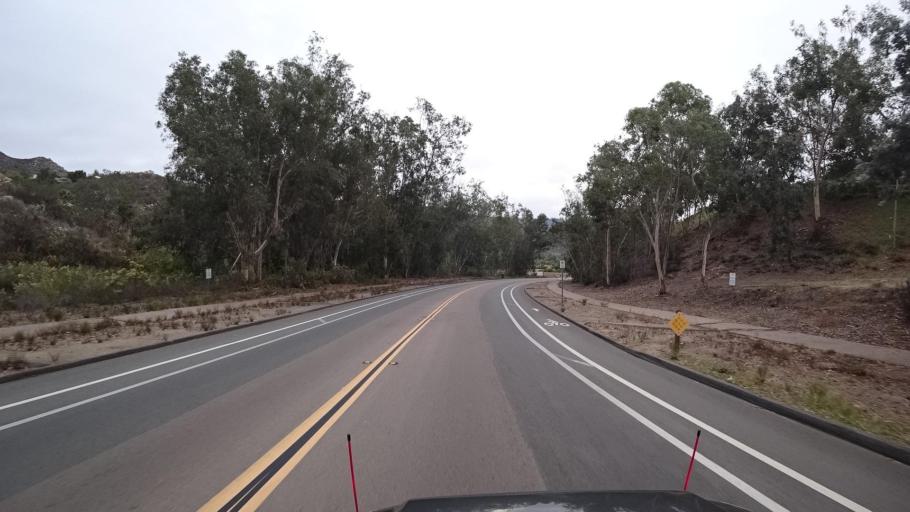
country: US
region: California
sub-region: San Diego County
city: Rancho San Diego
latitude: 32.7611
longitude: -116.9081
